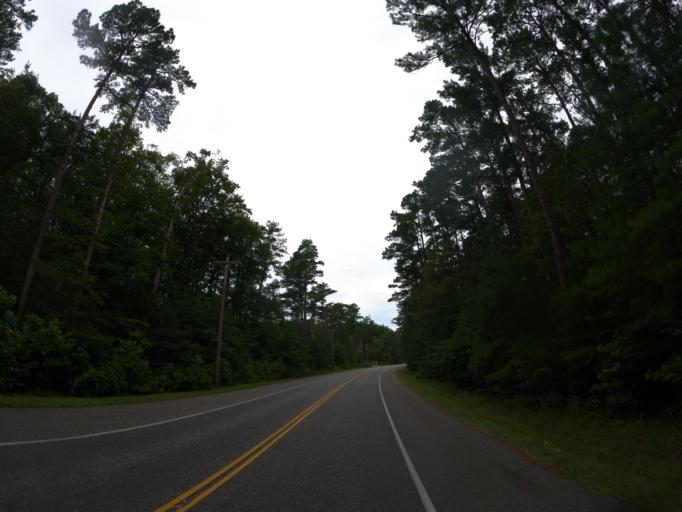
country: US
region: Maryland
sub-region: Saint Mary's County
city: California
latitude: 38.2532
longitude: -76.5109
